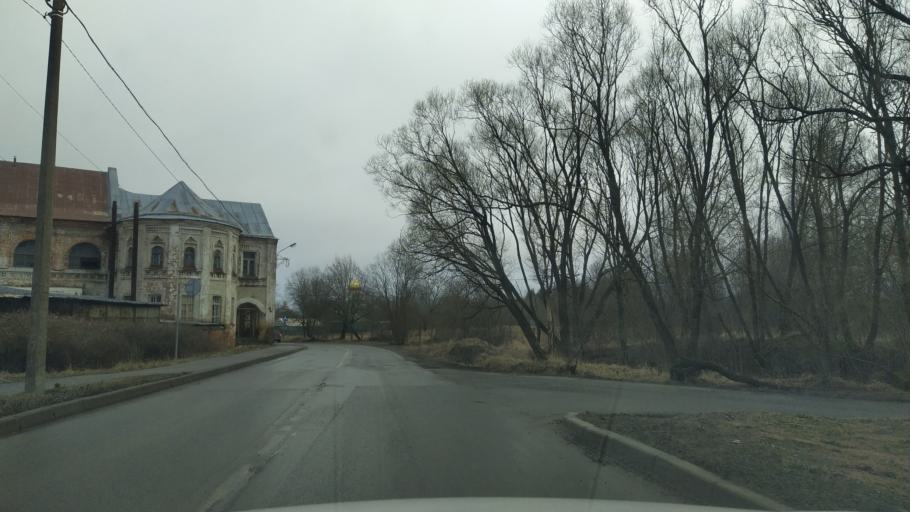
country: RU
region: St.-Petersburg
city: Pushkin
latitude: 59.7293
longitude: 30.3860
